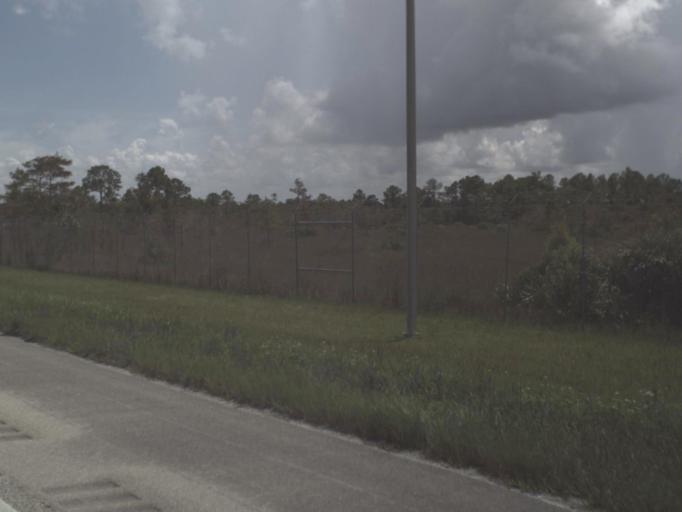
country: US
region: Florida
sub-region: Collier County
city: Immokalee
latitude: 26.1668
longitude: -81.2019
